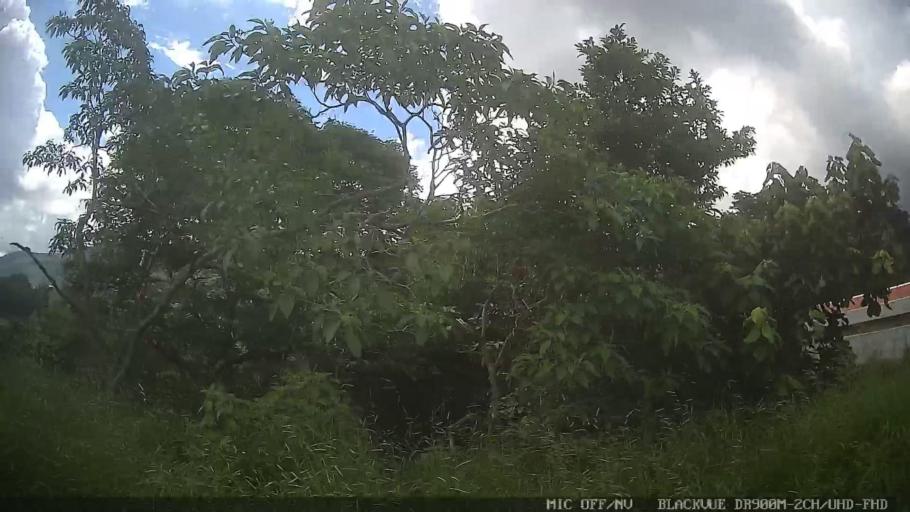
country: BR
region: Minas Gerais
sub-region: Extrema
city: Extrema
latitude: -22.8666
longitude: -46.3399
